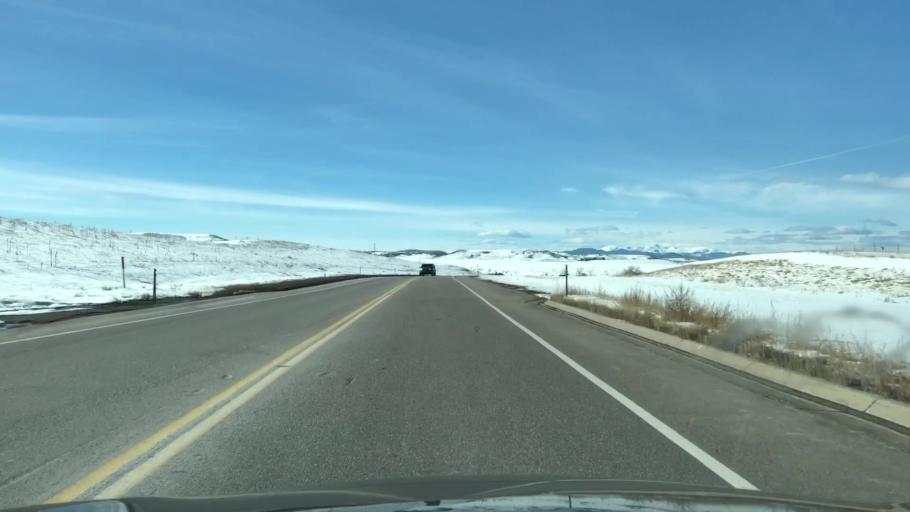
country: US
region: Colorado
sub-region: Douglas County
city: Stonegate
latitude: 39.5216
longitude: -104.8309
